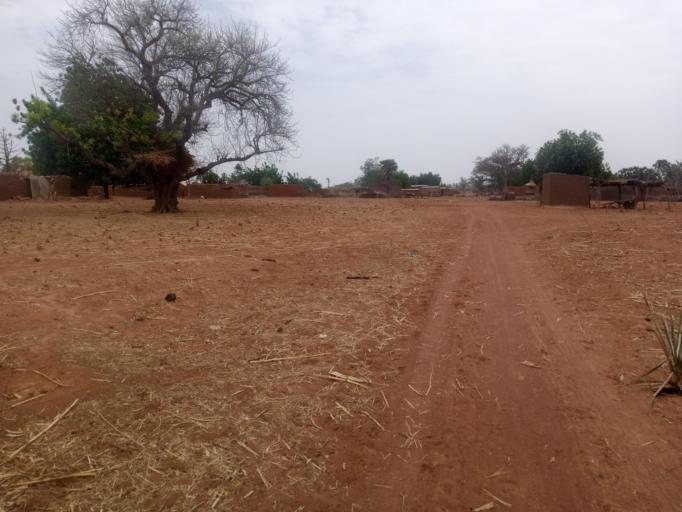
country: BF
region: Boucle du Mouhoun
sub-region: Province de la Kossi
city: Nouna
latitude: 12.8543
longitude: -4.0755
